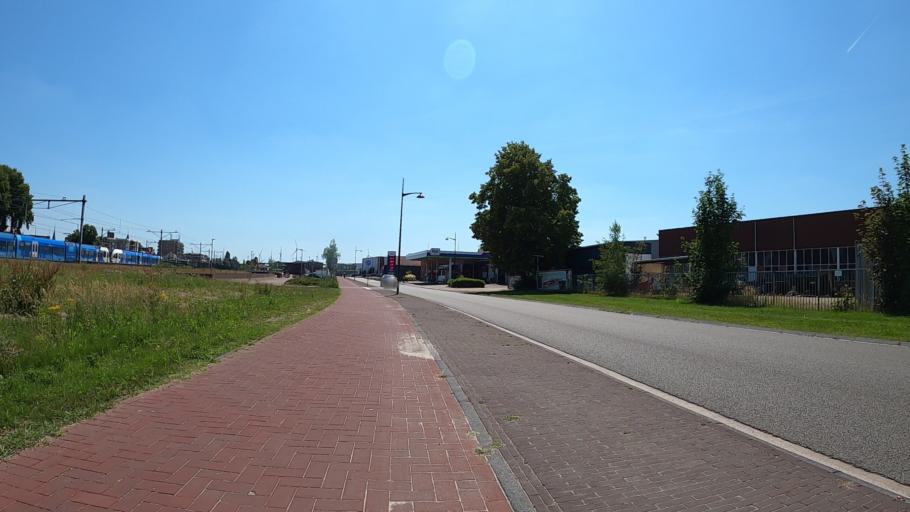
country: NL
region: Drenthe
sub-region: Gemeente Coevorden
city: Coevorden
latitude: 52.6654
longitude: 6.7349
